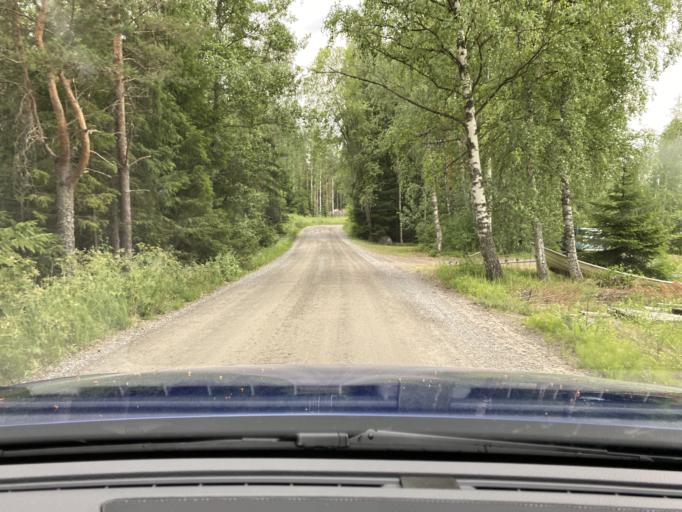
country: FI
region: Satakunta
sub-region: Rauma
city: Lappi
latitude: 61.1395
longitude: 21.9071
